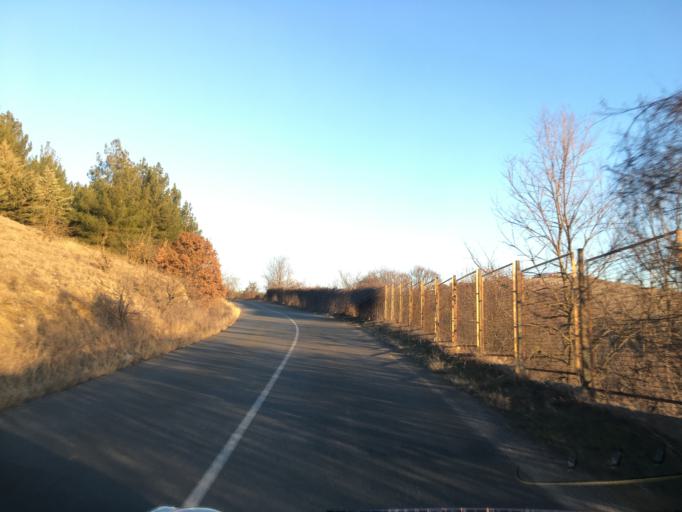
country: GR
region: West Macedonia
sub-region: Nomos Kozanis
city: Koila
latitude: 40.3241
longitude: 21.7943
